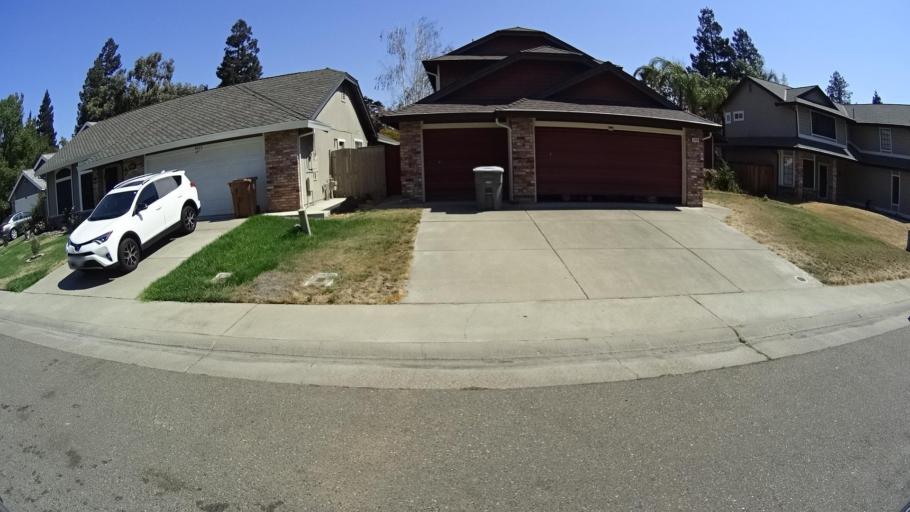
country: US
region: California
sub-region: Sacramento County
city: Laguna
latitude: 38.4139
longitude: -121.4150
